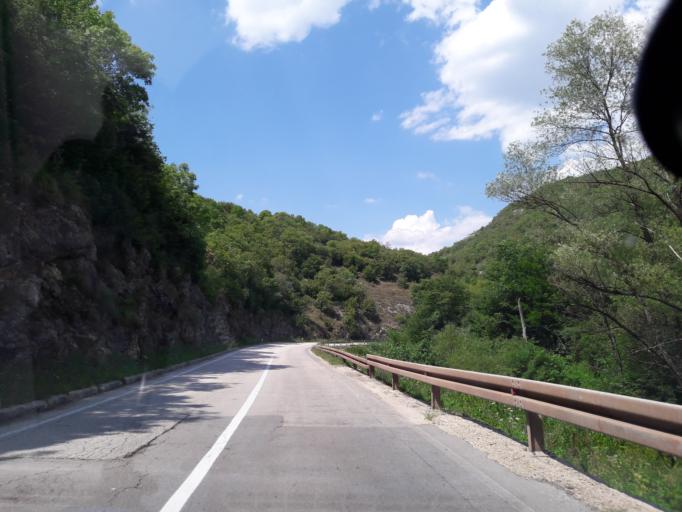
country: BA
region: Republika Srpska
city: Mrkonjic Grad
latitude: 44.4514
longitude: 17.1630
